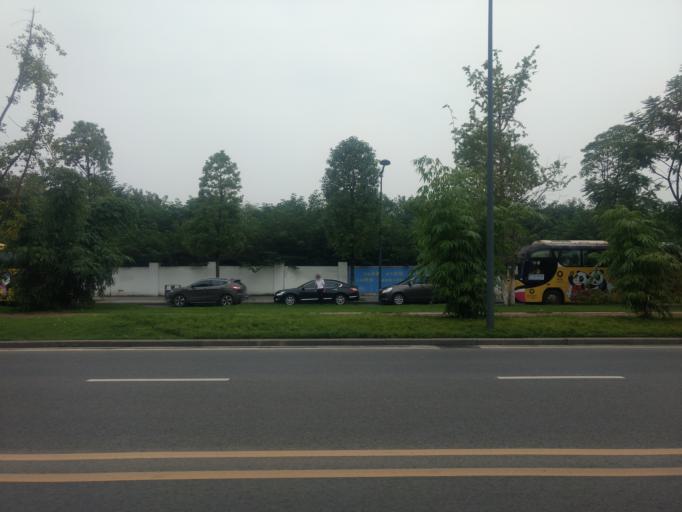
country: CN
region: Sichuan
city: Xindu
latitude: 30.7343
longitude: 104.1408
